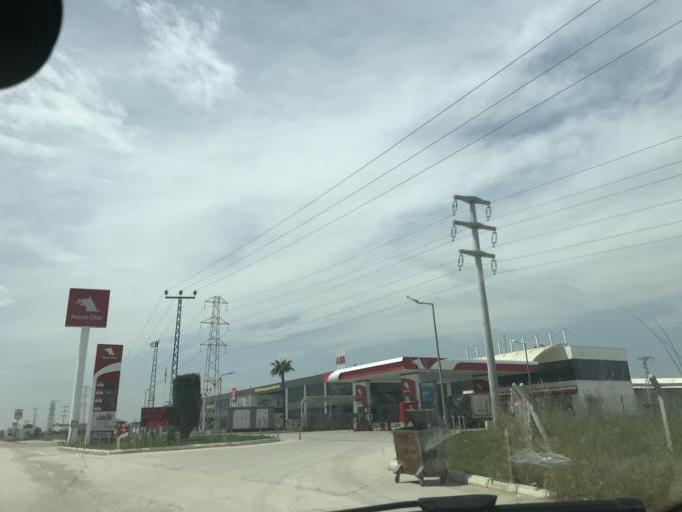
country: TR
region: Adana
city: Yuregir
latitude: 36.9826
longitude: 35.4187
